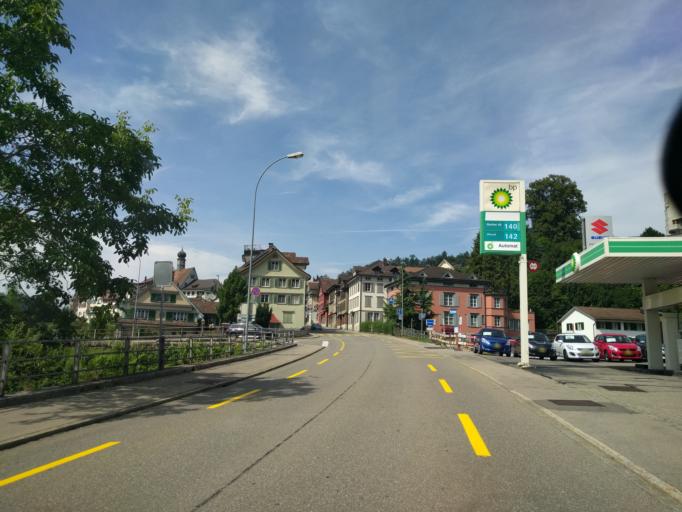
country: CH
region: Saint Gallen
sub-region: Wahlkreis Toggenburg
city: Lichtensteig
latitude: 47.3209
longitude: 9.0876
